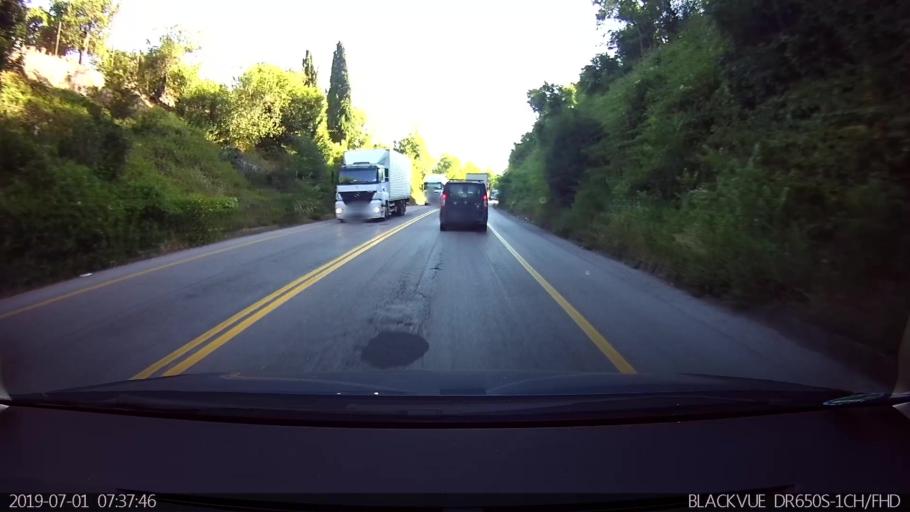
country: IT
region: Latium
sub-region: Provincia di Frosinone
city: Giuliano di Roma
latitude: 41.5402
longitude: 13.2673
